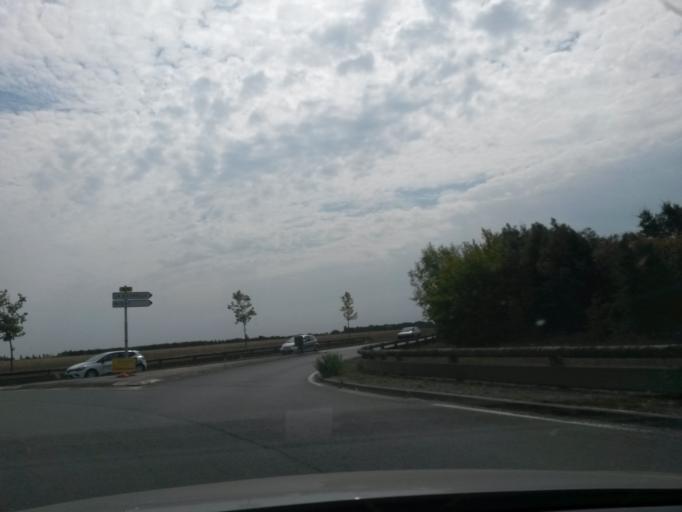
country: FR
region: Poitou-Charentes
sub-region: Departement de la Charente-Maritime
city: Saint-Xandre
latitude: 46.1951
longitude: -1.0955
